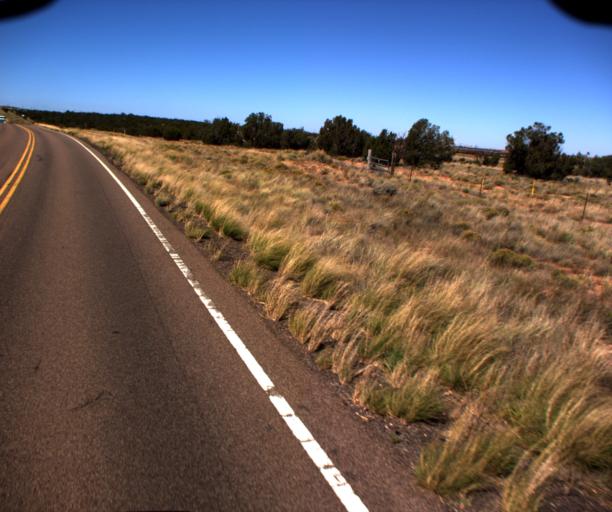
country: US
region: Arizona
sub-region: Navajo County
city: Taylor
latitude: 34.4826
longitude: -110.3055
